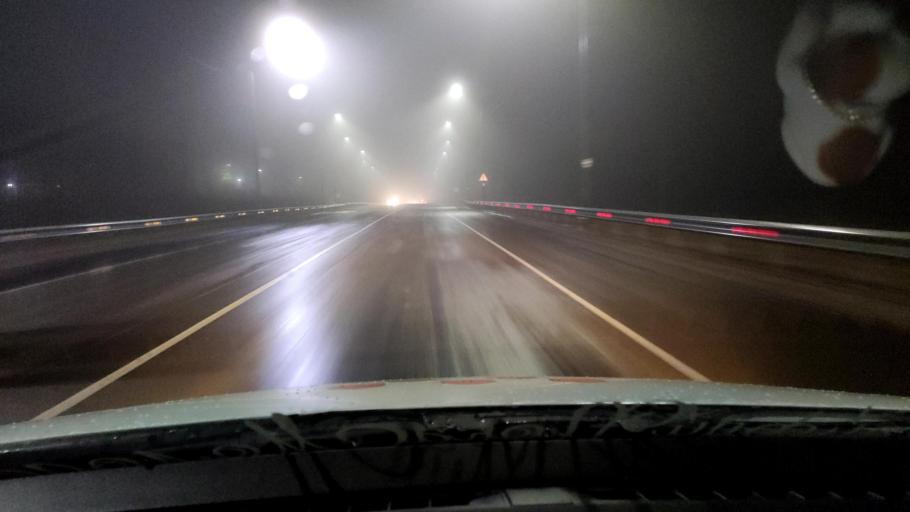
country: RU
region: Voronezj
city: Devitsa
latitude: 51.6329
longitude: 38.9654
